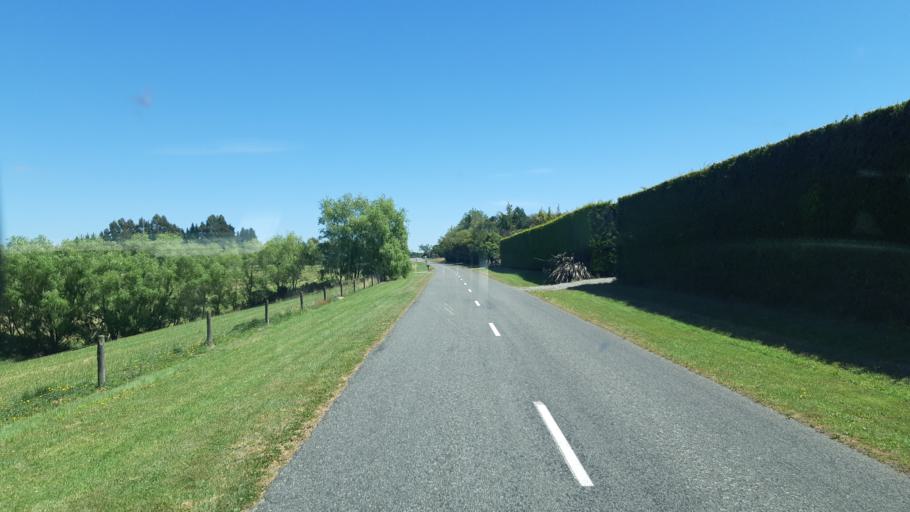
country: NZ
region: Canterbury
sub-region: Timaru District
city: Timaru
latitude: -44.3940
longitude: 171.1450
